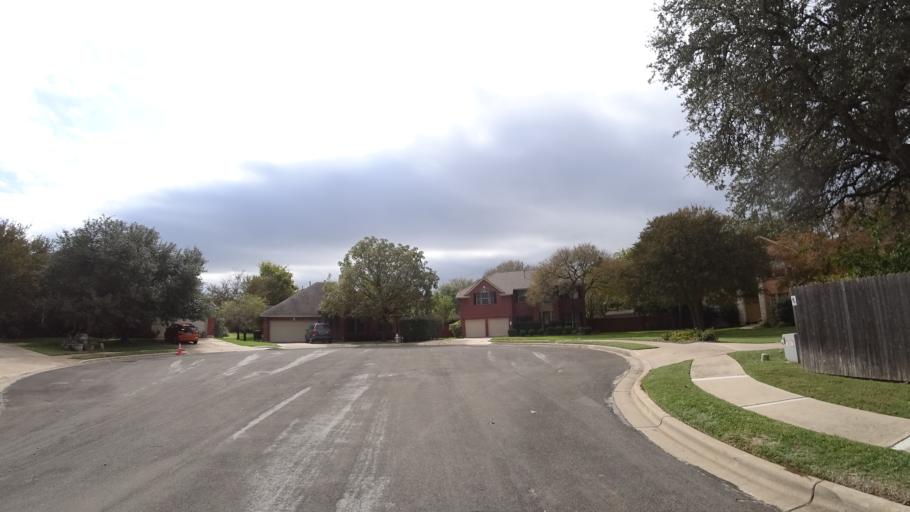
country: US
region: Texas
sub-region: Travis County
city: Shady Hollow
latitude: 30.1561
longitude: -97.8527
